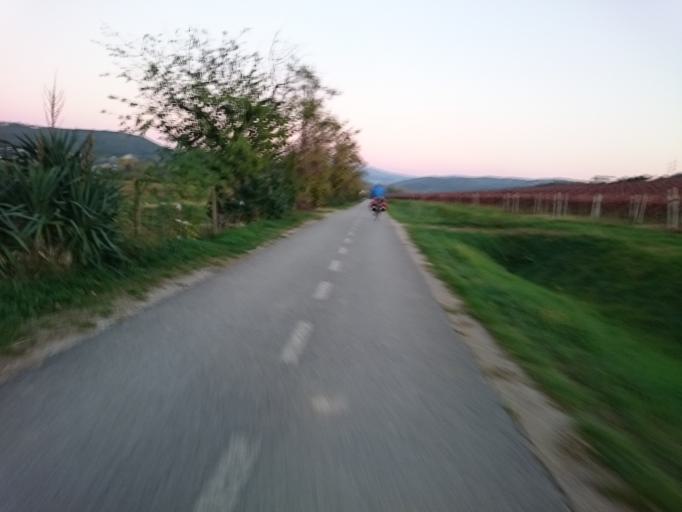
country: SI
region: Koper-Capodistria
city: Prade
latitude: 45.5496
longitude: 13.7770
